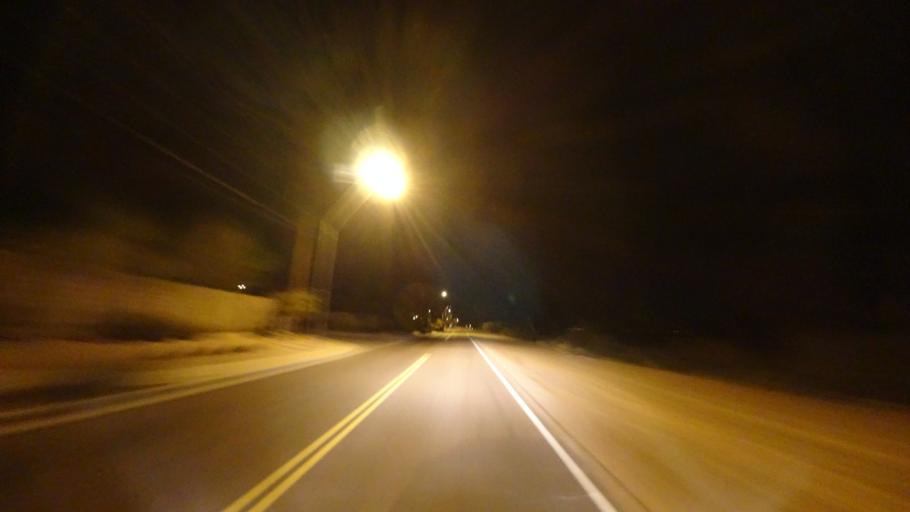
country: US
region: Arizona
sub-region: Pinal County
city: Apache Junction
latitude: 33.3788
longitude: -111.5223
